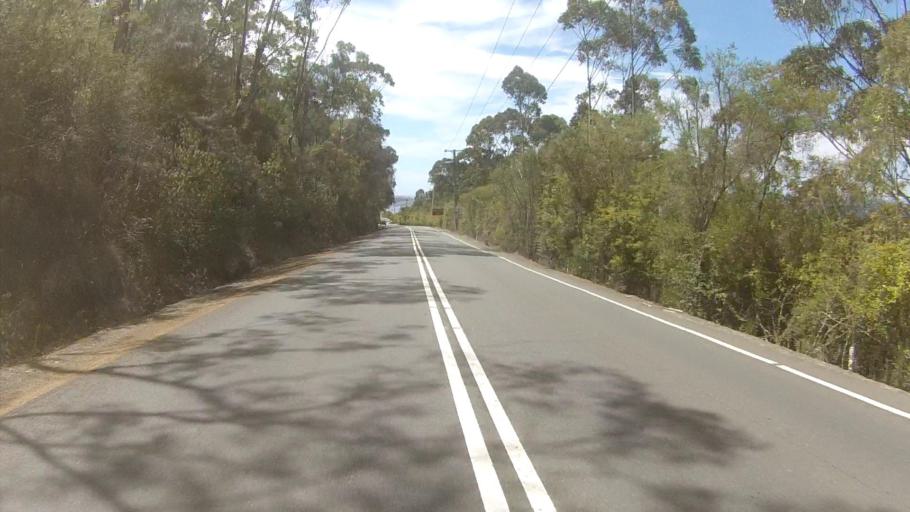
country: AU
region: Tasmania
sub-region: Kingborough
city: Taroona
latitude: -42.9594
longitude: 147.3340
